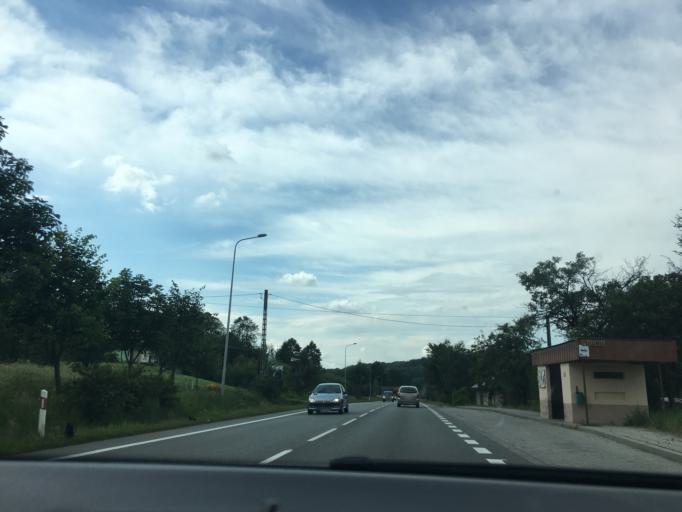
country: PL
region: Subcarpathian Voivodeship
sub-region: Powiat strzyzowski
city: Polomia
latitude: 49.8909
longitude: 21.8941
